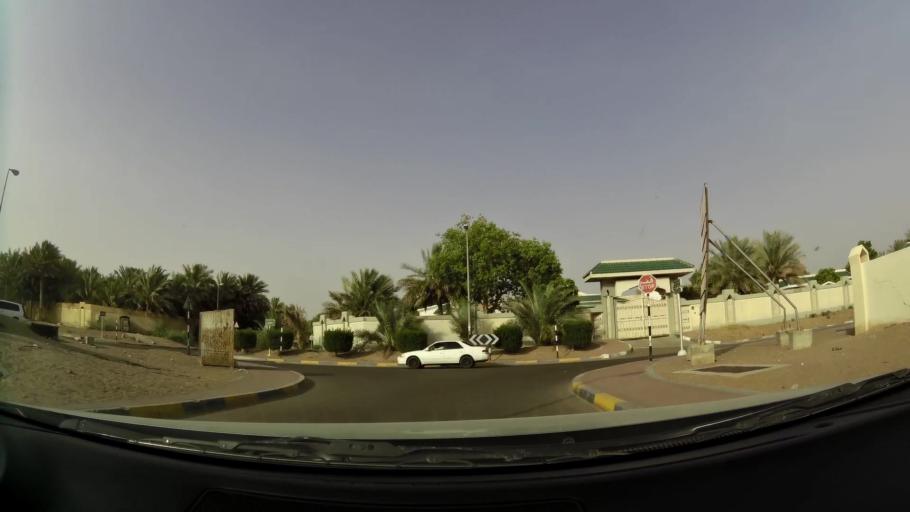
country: AE
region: Abu Dhabi
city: Al Ain
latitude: 24.2188
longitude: 55.6498
